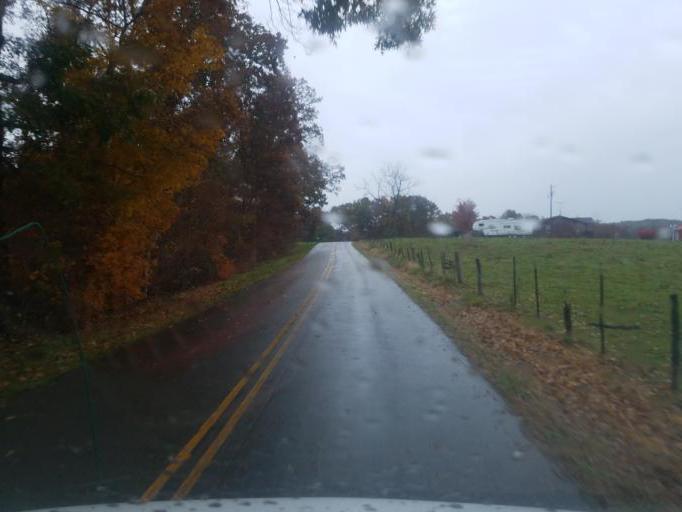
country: US
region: West Virginia
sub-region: Wood County
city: Vienna
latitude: 39.4157
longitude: -81.6108
